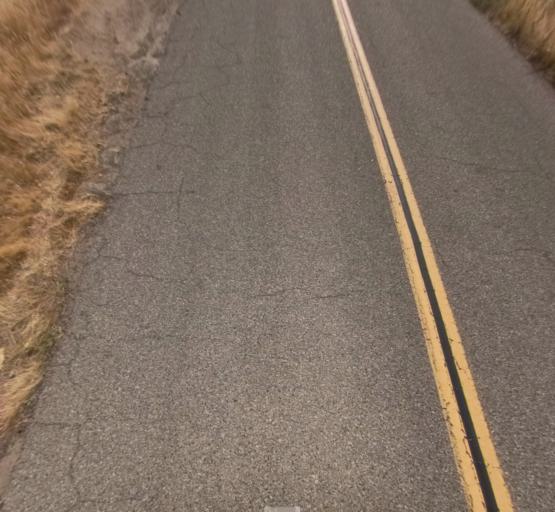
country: US
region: California
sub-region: Madera County
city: Bonadelle Ranchos-Madera Ranchos
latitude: 37.0278
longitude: -119.7212
